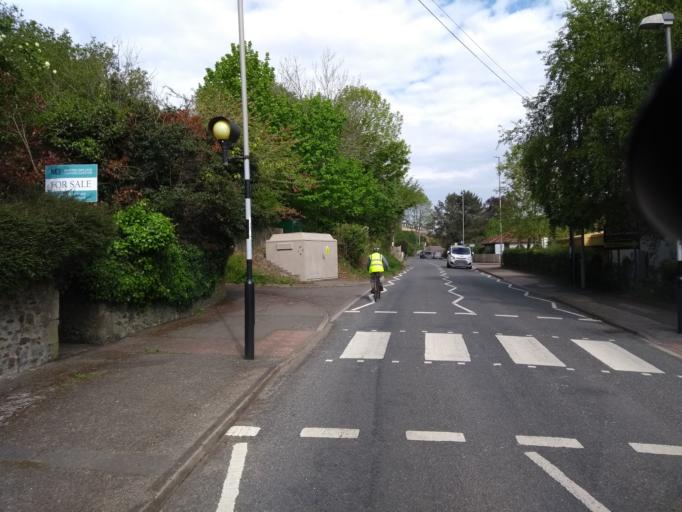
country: GB
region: England
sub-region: Dorset
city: Lyme Regis
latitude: 50.7295
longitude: -2.9467
